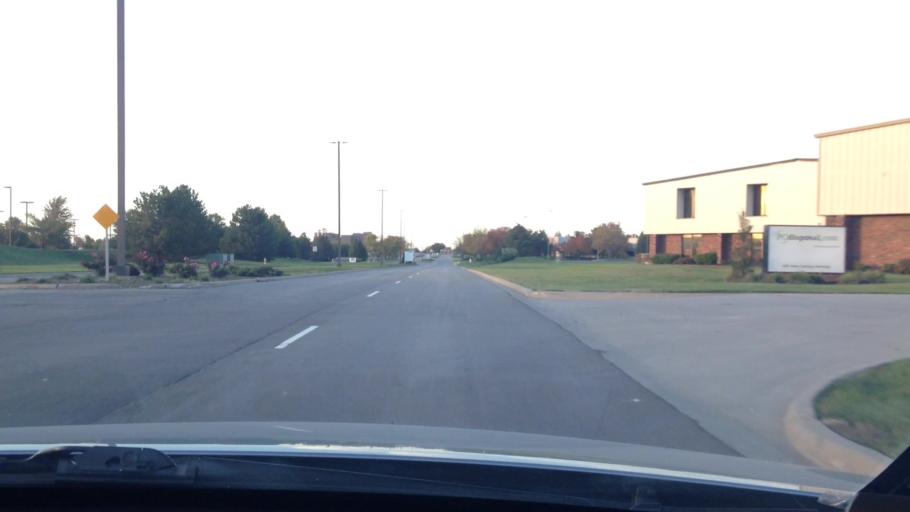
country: US
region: Kansas
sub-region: Johnson County
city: Gardner
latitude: 38.8255
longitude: -94.8992
